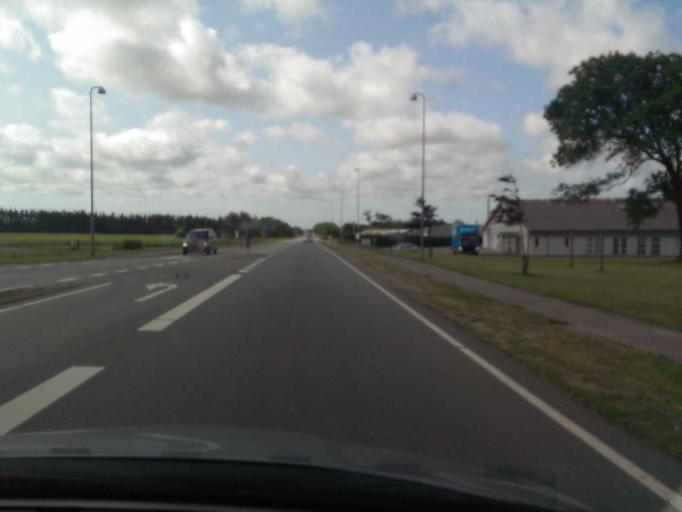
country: DK
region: North Denmark
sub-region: Bronderslev Kommune
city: Bronderslev
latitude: 57.2667
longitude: 9.9695
